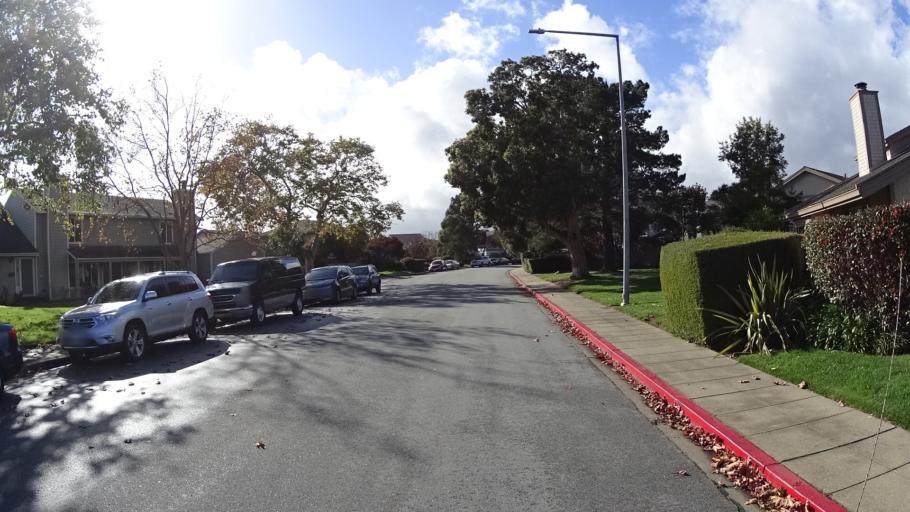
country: US
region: California
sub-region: San Mateo County
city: Foster City
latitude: 37.5509
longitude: -122.2696
